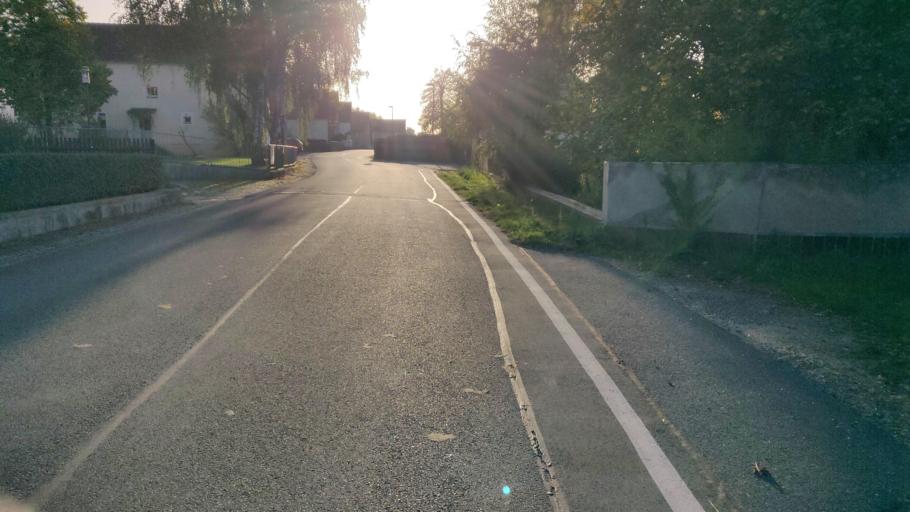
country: DE
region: Brandenburg
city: Hirschfeld
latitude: 51.3401
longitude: 13.5866
